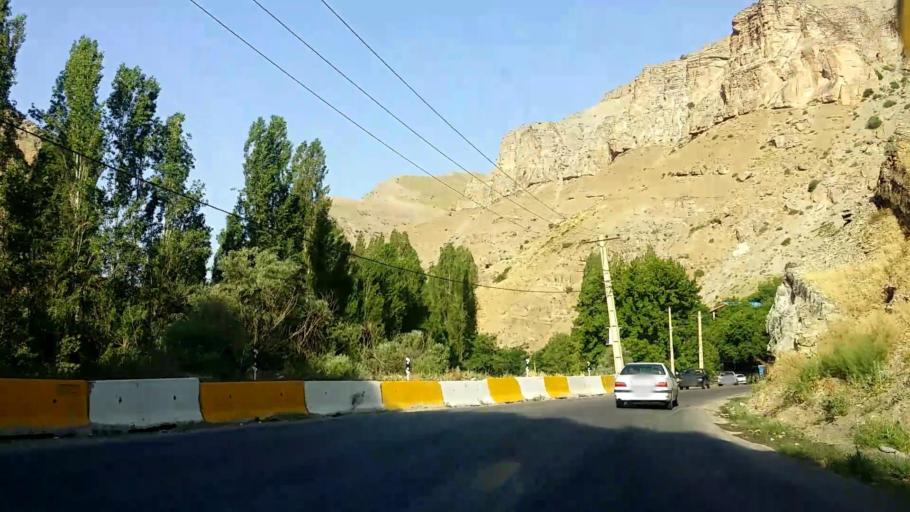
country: IR
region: Alborz
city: Karaj
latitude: 36.0233
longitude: 51.1557
